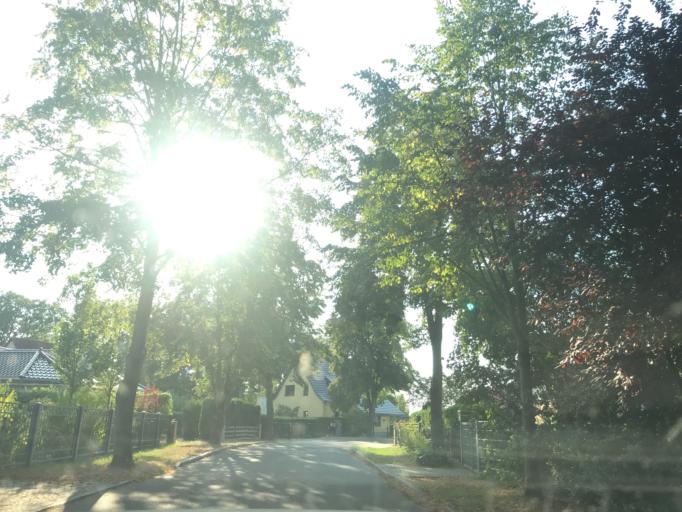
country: DE
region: Brandenburg
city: Potsdam
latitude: 52.4434
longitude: 13.0316
